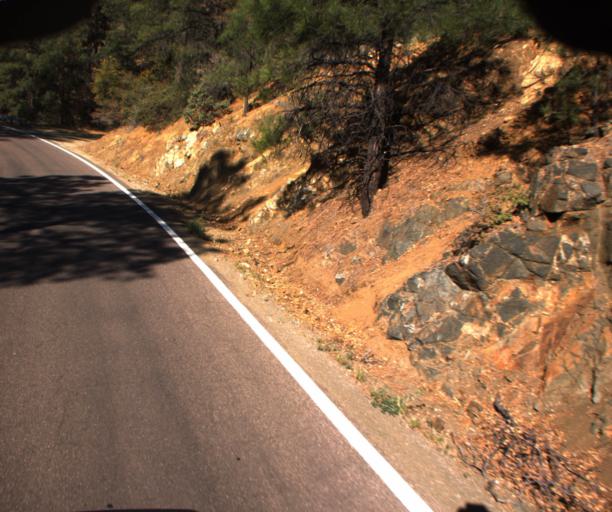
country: US
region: Arizona
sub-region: Yavapai County
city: Prescott
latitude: 34.4850
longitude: -112.5034
